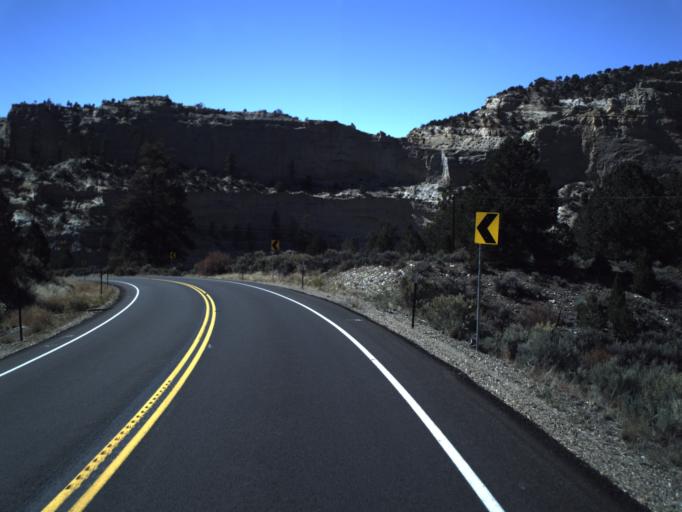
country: US
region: Utah
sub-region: Garfield County
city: Panguitch
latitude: 37.6166
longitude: -111.8921
